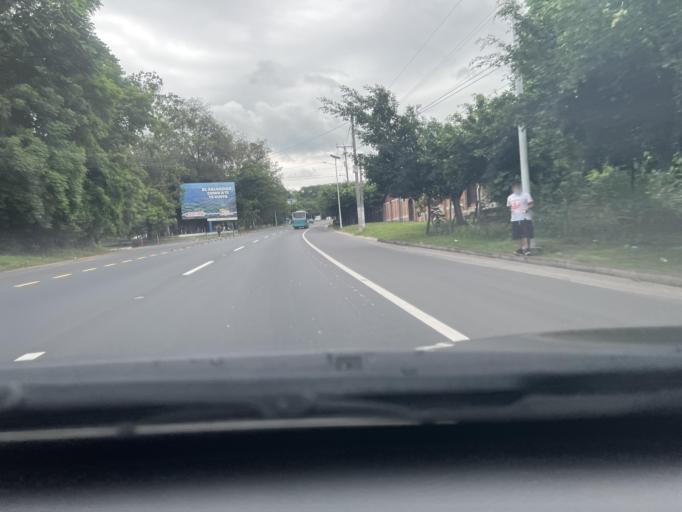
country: SV
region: Santa Ana
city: El Congo
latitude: 13.8848
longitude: -89.4955
